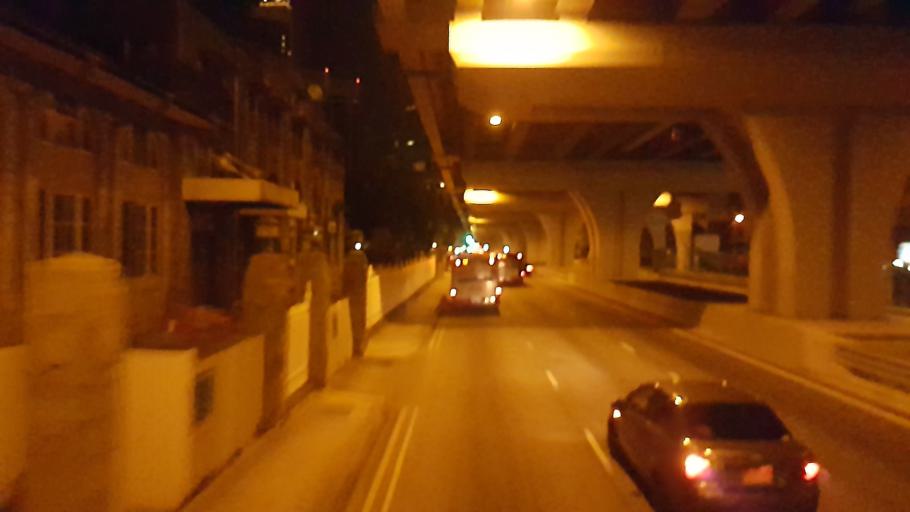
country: SG
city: Singapore
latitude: 1.2725
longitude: 103.8380
